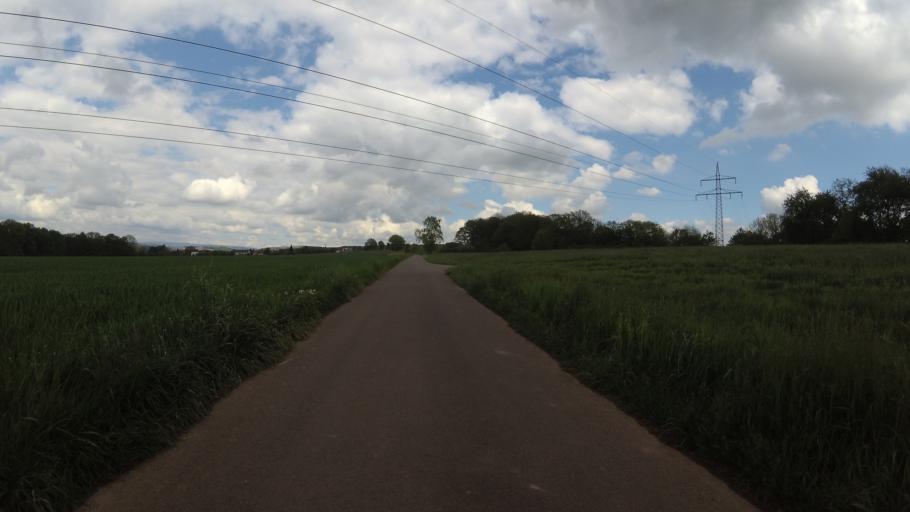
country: DE
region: Saarland
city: Schmelz
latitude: 49.4003
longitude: 6.8573
